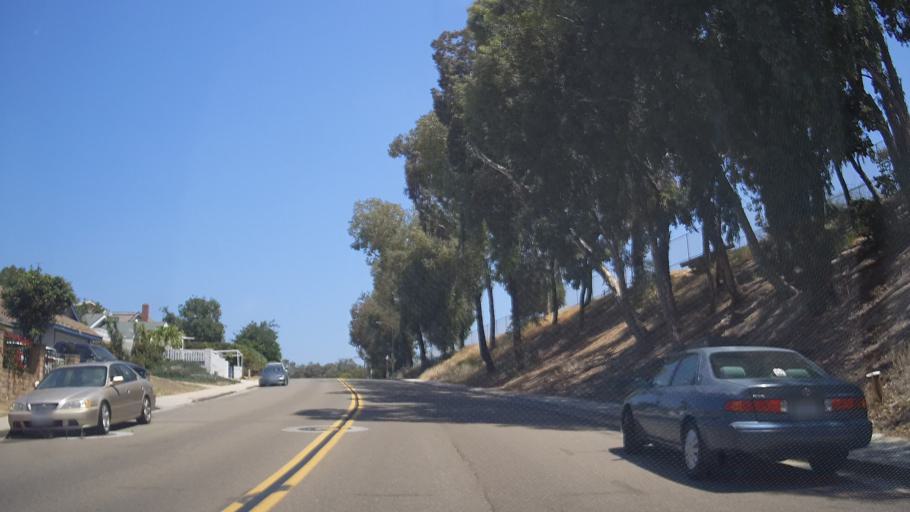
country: US
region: California
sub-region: San Diego County
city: Bonita
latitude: 32.6761
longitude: -117.0485
